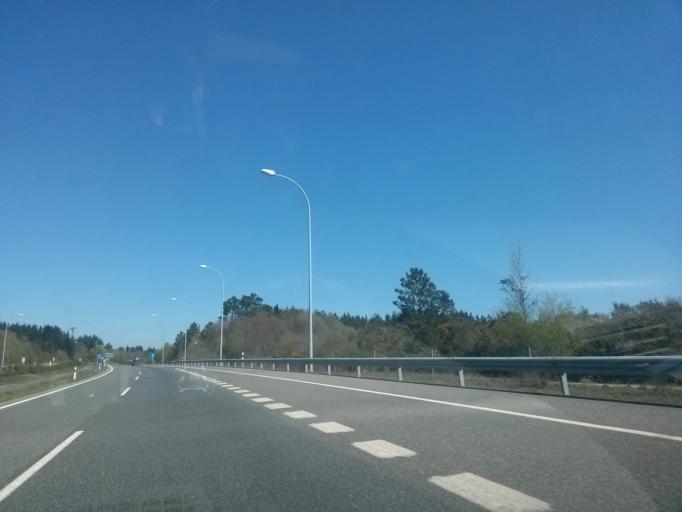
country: ES
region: Galicia
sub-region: Provincia de Lugo
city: Lugo
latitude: 43.0190
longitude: -7.5201
